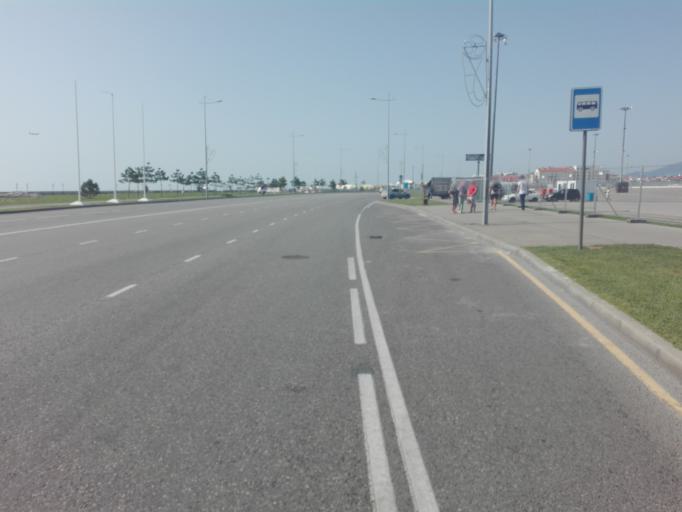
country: RU
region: Krasnodarskiy
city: Adler
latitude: 43.4002
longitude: 39.9503
